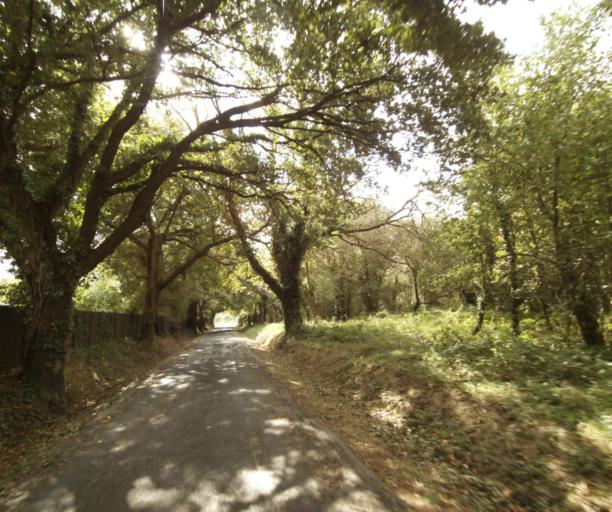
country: FR
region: Languedoc-Roussillon
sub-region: Departement des Pyrenees-Orientales
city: Argelers
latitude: 42.5640
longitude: 3.0305
